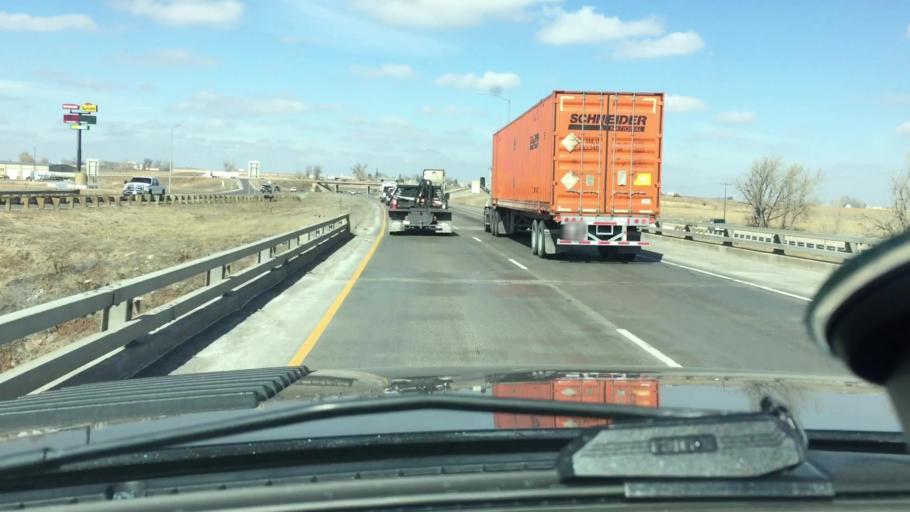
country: US
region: Colorado
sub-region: Weld County
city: Mead
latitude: 40.3018
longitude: -104.9815
